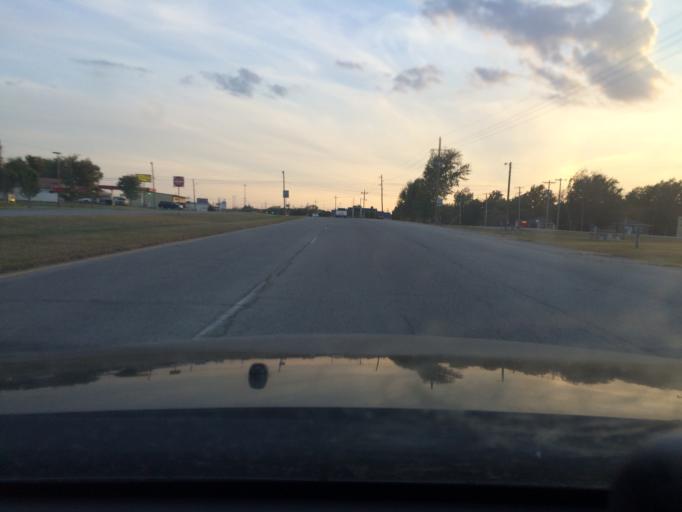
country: US
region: Oklahoma
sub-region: Rogers County
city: Catoosa
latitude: 36.1808
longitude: -95.7485
